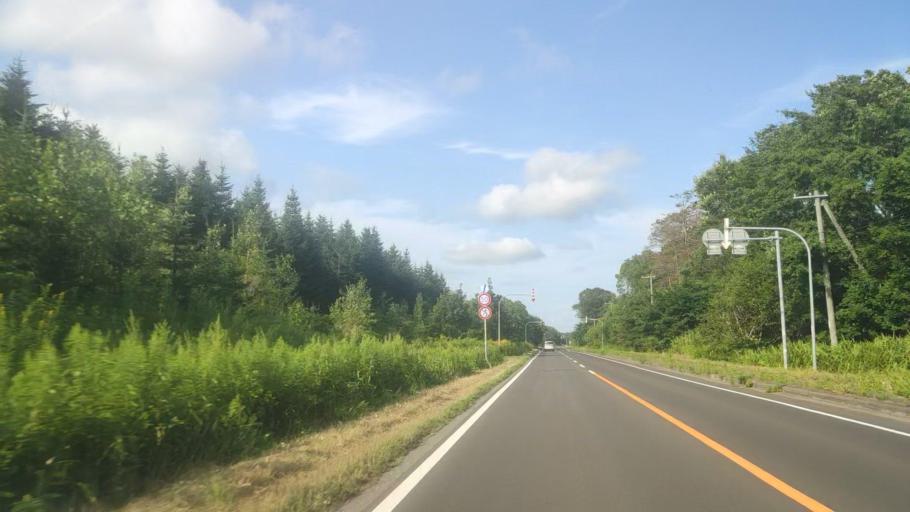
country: JP
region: Hokkaido
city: Chitose
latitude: 42.7361
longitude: 141.7785
